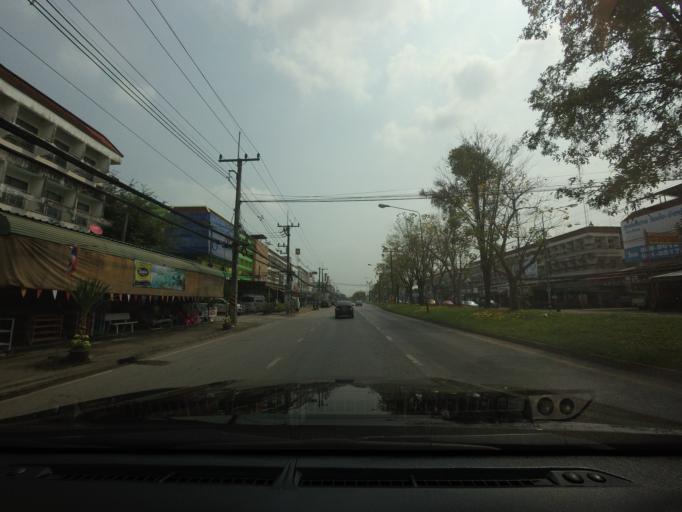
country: TH
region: Nakhon Nayok
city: Nakhon Nayok
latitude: 14.2119
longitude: 101.2037
